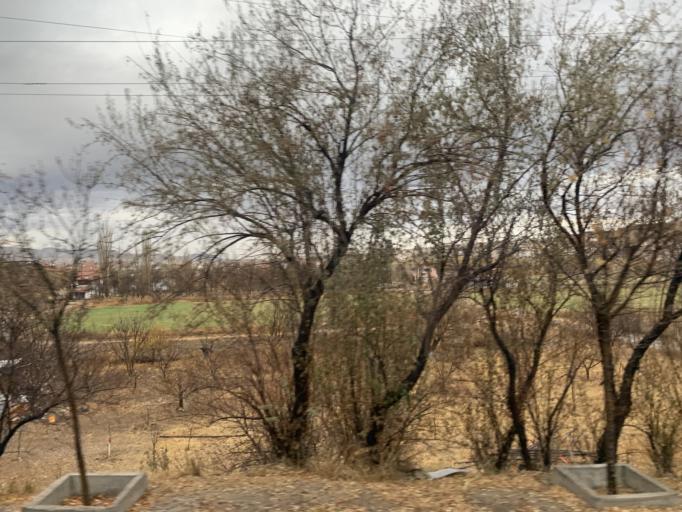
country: TR
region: Nevsehir
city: Avanos
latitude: 38.7147
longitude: 34.8590
